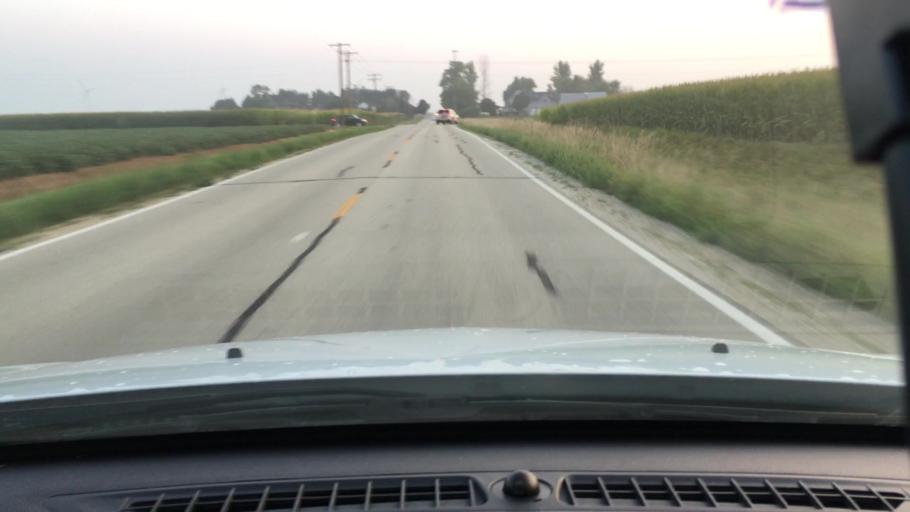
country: US
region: Illinois
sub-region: DeKalb County
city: Malta
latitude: 41.8623
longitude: -88.8479
